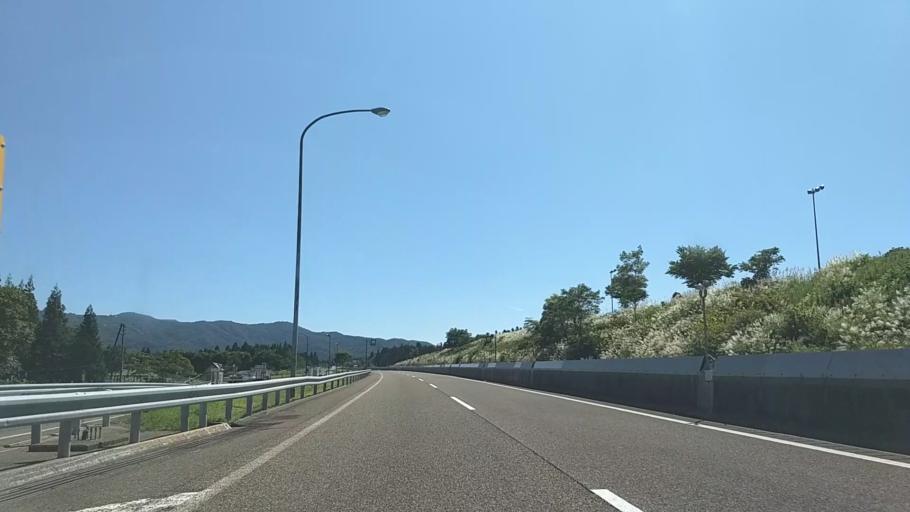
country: JP
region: Niigata
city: Arai
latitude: 36.9306
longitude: 138.2122
